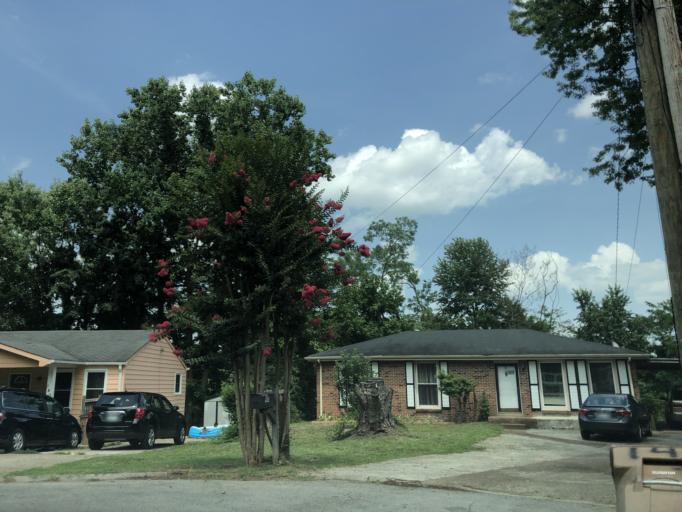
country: US
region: Tennessee
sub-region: Williamson County
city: Brentwood Estates
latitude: 36.0603
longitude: -86.6890
